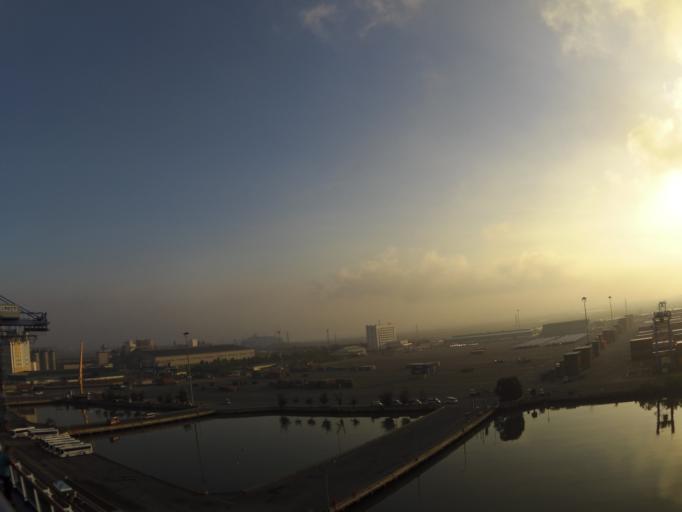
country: VN
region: Ba Ria-Vung Tau
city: Thi Tran Phu My
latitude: 10.5390
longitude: 107.0285
